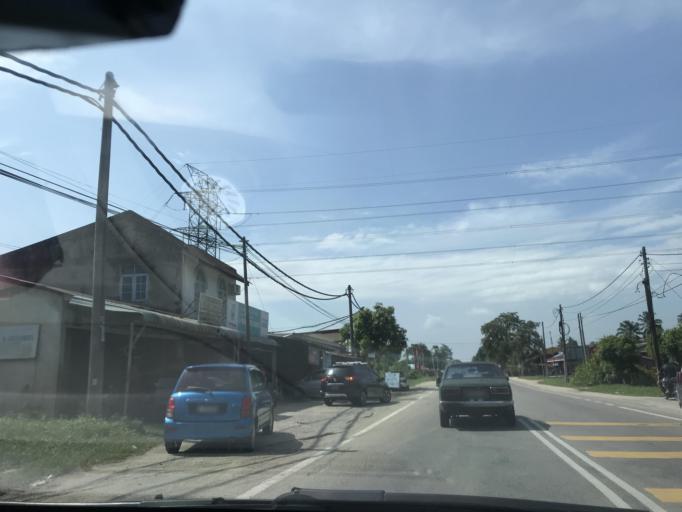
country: MY
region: Kelantan
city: Tumpat
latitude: 6.1485
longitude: 102.1621
